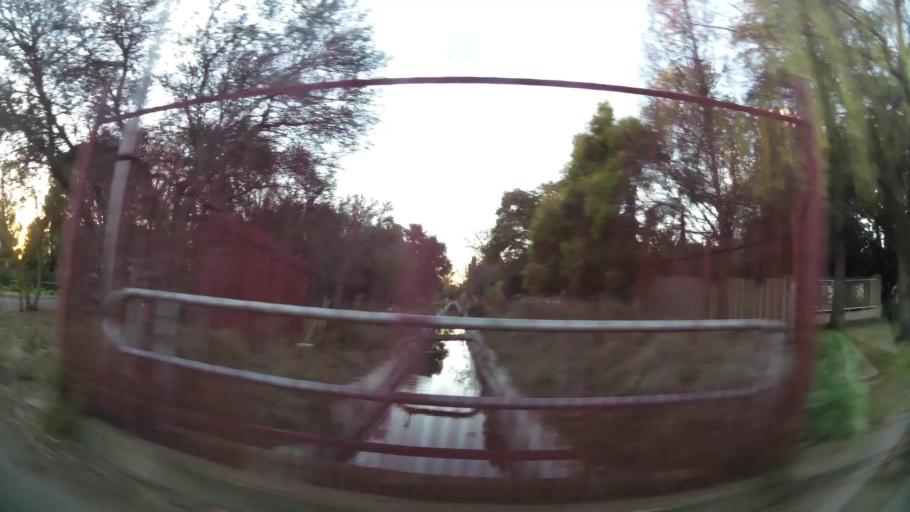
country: ZA
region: North-West
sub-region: Dr Kenneth Kaunda District Municipality
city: Potchefstroom
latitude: -26.7228
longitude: 27.1125
